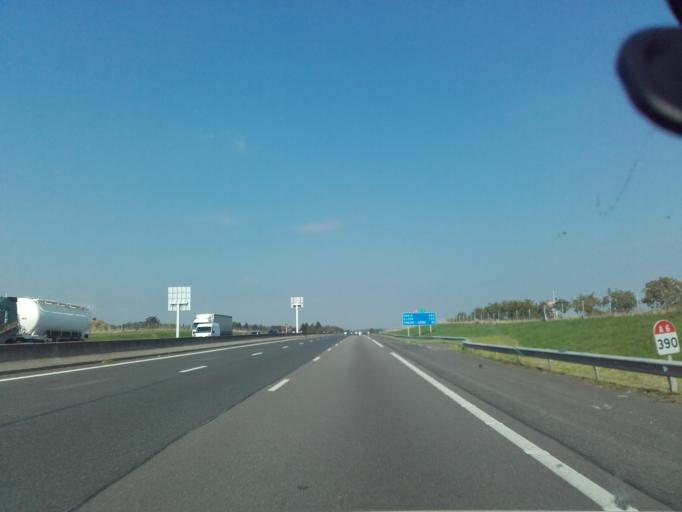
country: FR
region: Bourgogne
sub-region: Departement de Saone-et-Loire
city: Charnay-les-Macon
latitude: 46.2958
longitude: 4.7919
